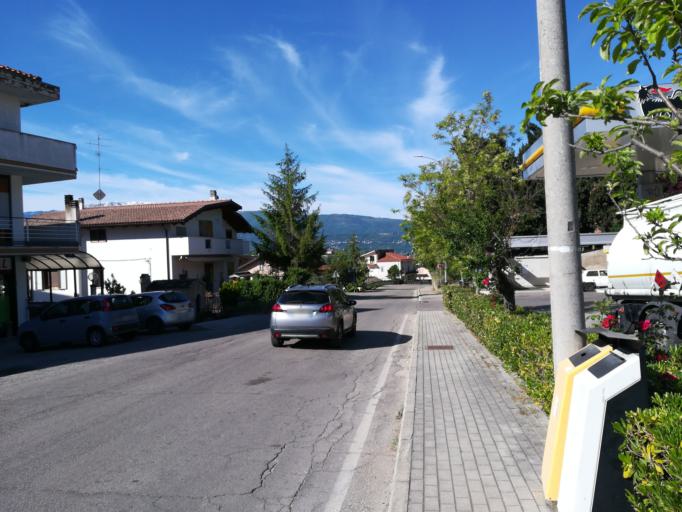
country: IT
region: Abruzzo
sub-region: Provincia di Chieti
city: Bucchianico
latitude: 42.3014
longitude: 14.1812
